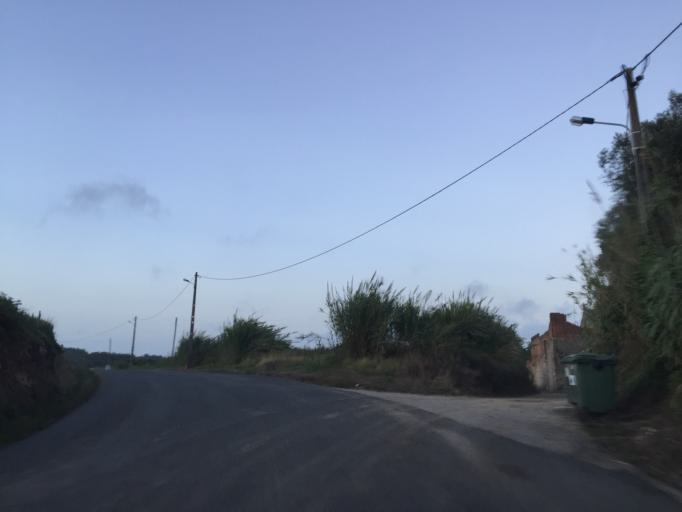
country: PT
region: Leiria
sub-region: Bombarral
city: Bombarral
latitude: 39.2887
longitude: -9.2103
